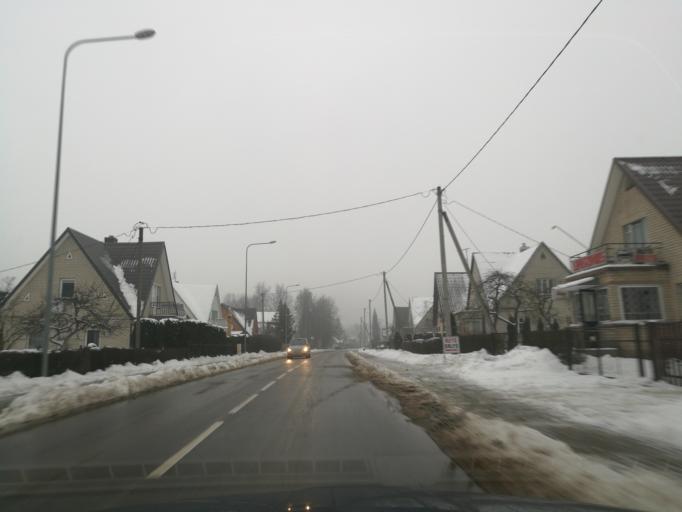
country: LT
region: Utenos apskritis
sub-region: Anyksciai
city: Anyksciai
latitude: 55.5167
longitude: 25.0924
